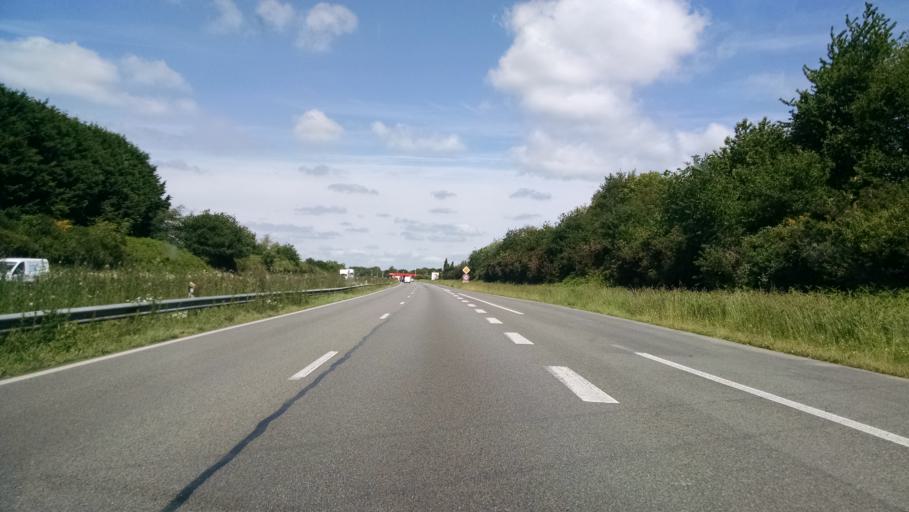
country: FR
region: Pays de la Loire
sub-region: Departement de la Loire-Atlantique
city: Le Temple-de-Bretagne
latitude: 47.3255
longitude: -1.7793
